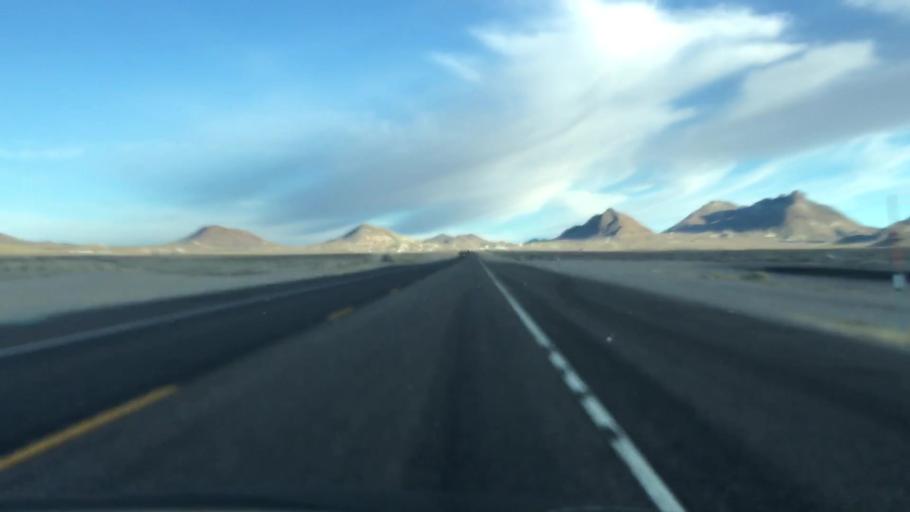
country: US
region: Nevada
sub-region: Nye County
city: Tonopah
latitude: 38.0858
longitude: -117.2839
